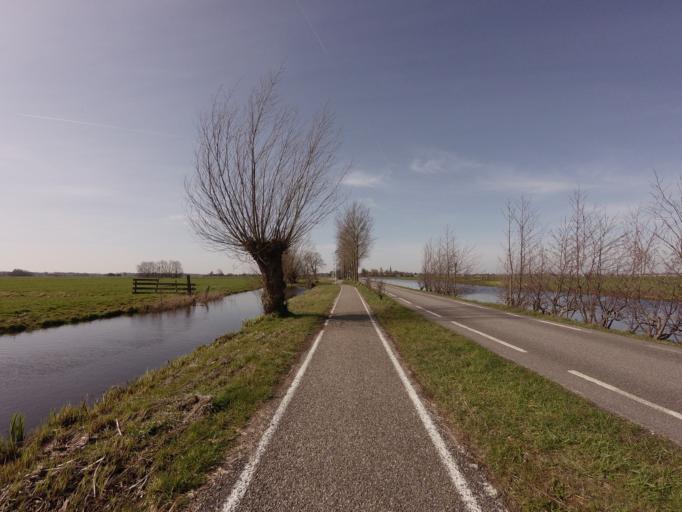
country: NL
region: South Holland
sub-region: Bodegraven-Reeuwijk
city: Reeuwijk
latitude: 52.0589
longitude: 4.7064
